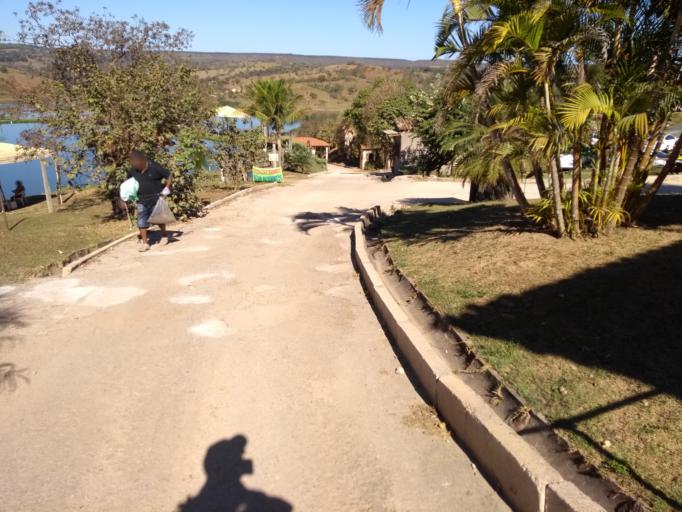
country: BR
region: Goias
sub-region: Luziania
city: Luziania
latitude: -16.1182
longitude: -48.2913
